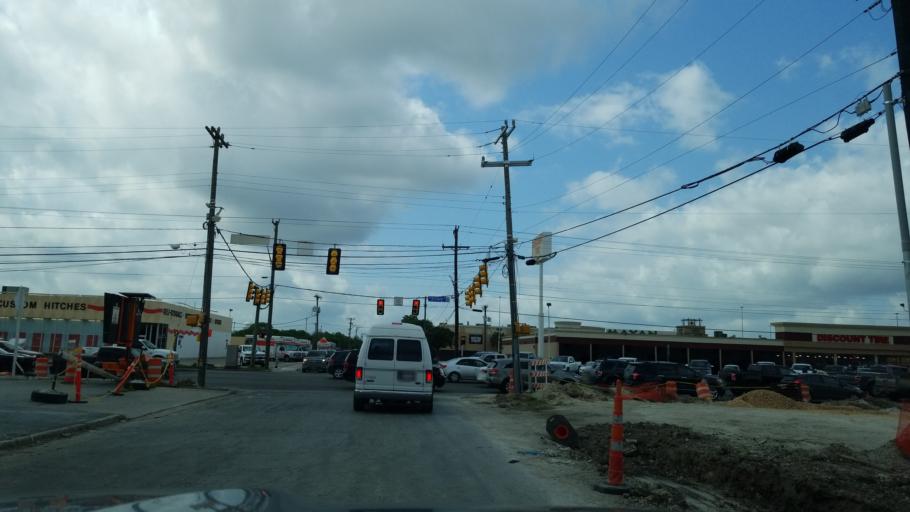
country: US
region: Texas
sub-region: Bexar County
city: San Antonio
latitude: 29.3571
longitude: -98.5231
